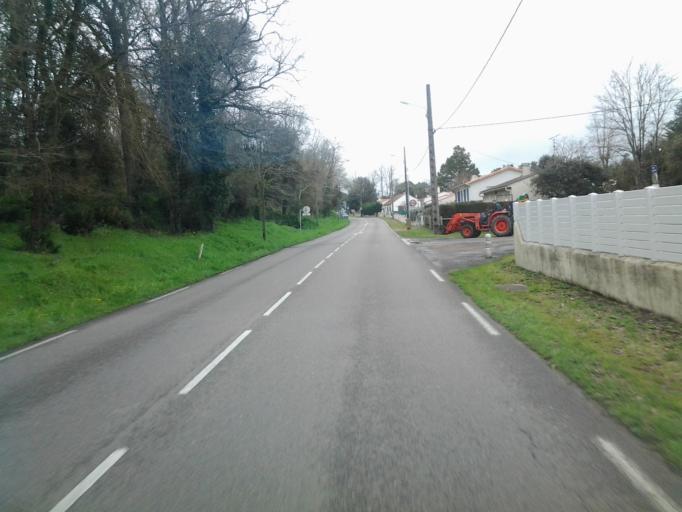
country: FR
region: Pays de la Loire
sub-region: Departement de la Vendee
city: Longeville-sur-Mer
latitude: 46.4066
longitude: -1.4910
